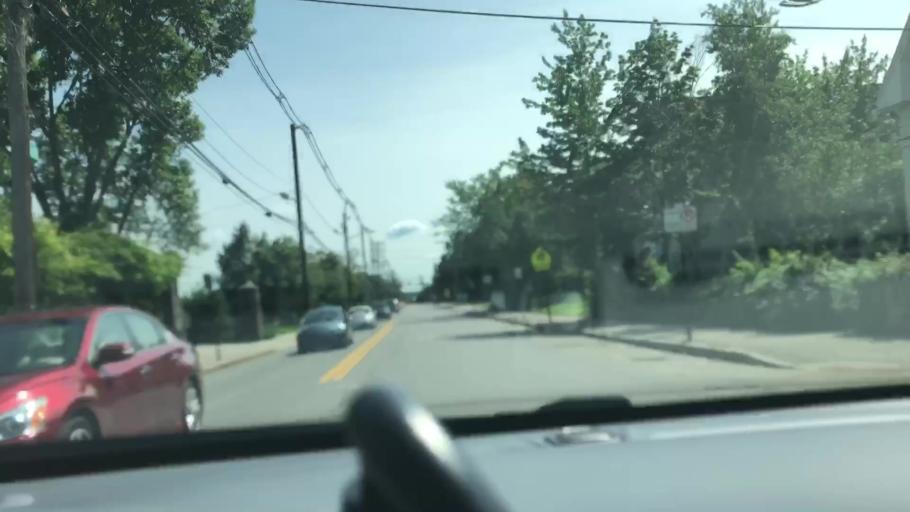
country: US
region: New Hampshire
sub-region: Hillsborough County
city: Manchester
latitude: 42.9879
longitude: -71.4740
